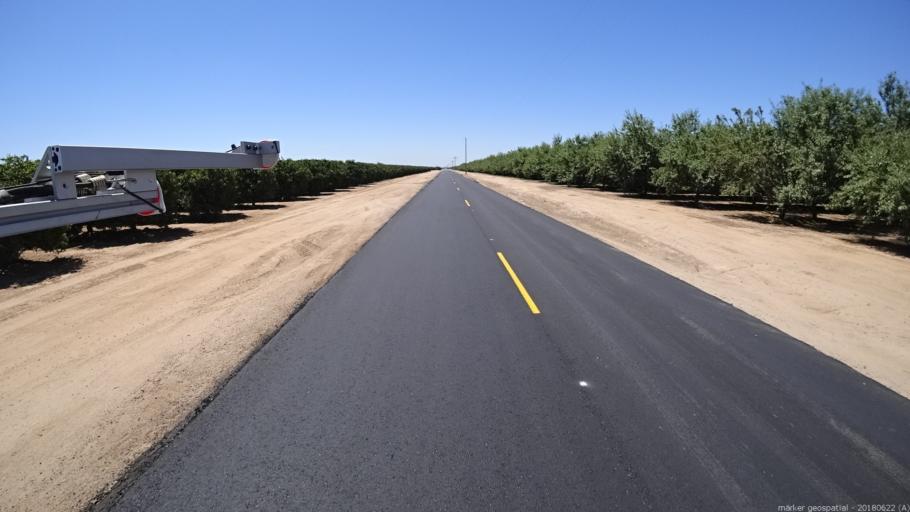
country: US
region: California
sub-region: Madera County
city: Bonadelle Ranchos-Madera Ranchos
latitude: 36.8982
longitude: -119.8576
